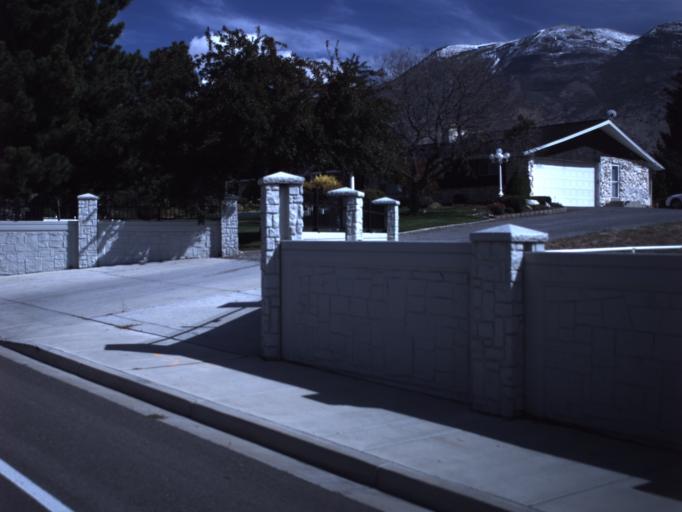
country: US
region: Utah
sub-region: Utah County
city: American Fork
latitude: 40.3867
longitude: -111.7690
